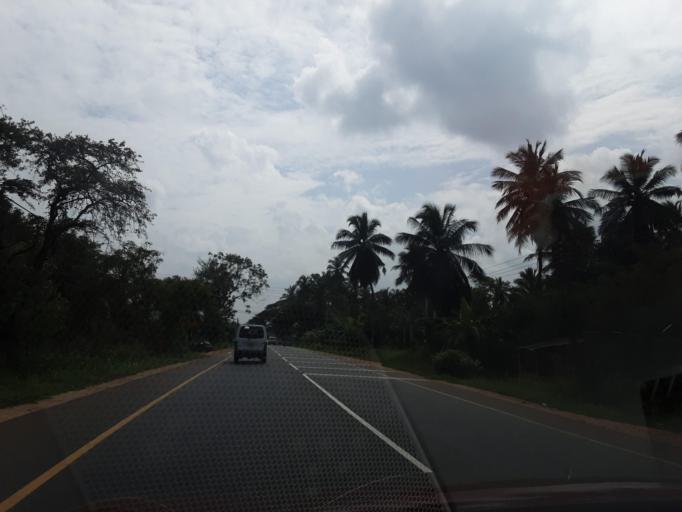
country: LK
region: North Central
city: Anuradhapura
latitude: 8.4776
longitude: 80.5127
